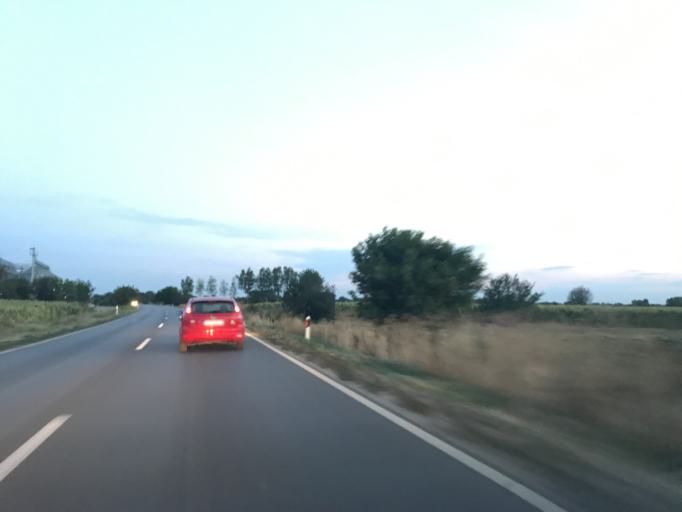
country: RS
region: Central Serbia
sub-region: Branicevski Okrug
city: Pozarevac
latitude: 44.6307
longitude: 21.1447
